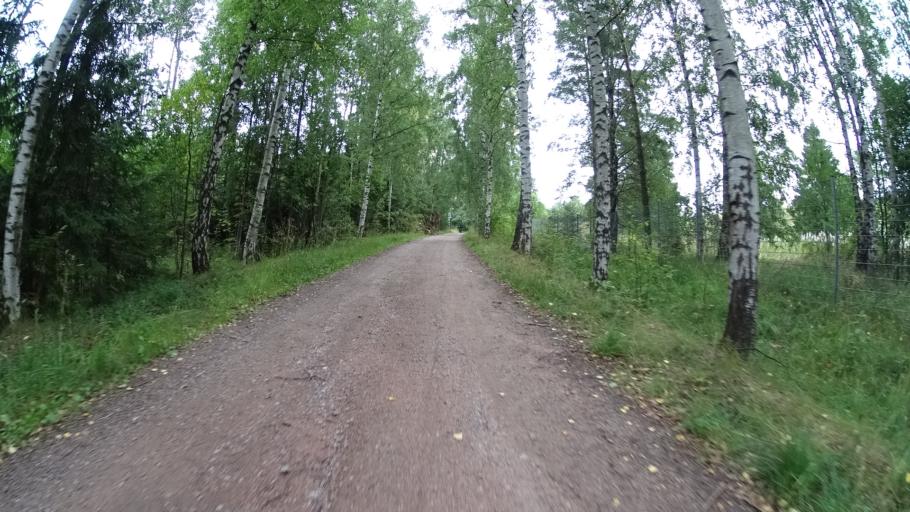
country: FI
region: Uusimaa
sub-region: Helsinki
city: Teekkarikylae
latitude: 60.2746
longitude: 24.8874
